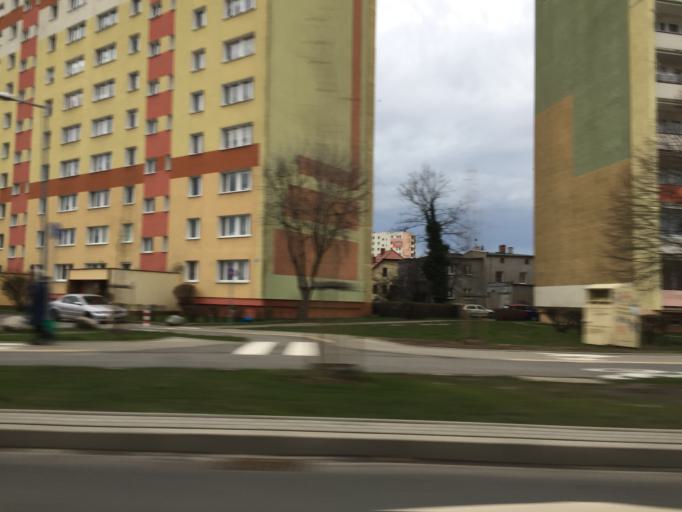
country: PL
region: Kujawsko-Pomorskie
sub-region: Bydgoszcz
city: Bydgoszcz
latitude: 53.1136
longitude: 18.0167
